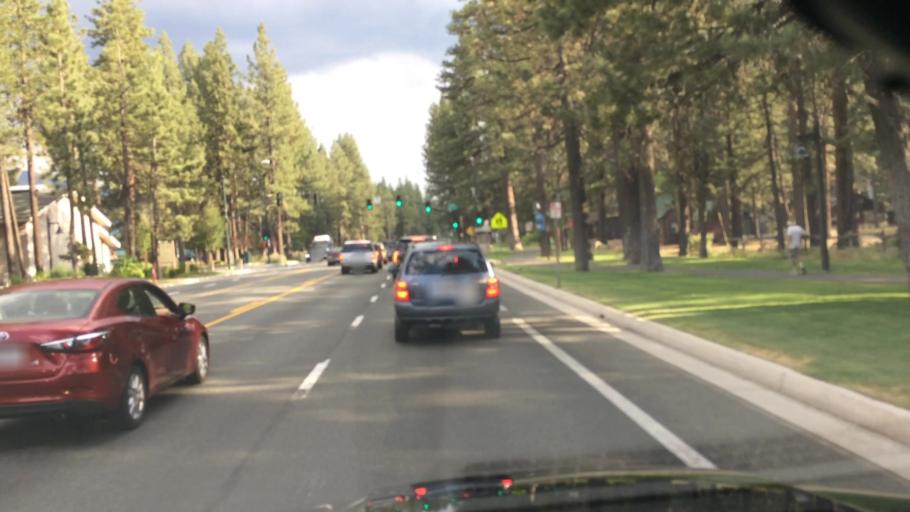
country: US
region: California
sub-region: El Dorado County
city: South Lake Tahoe
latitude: 38.9388
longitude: -119.9773
